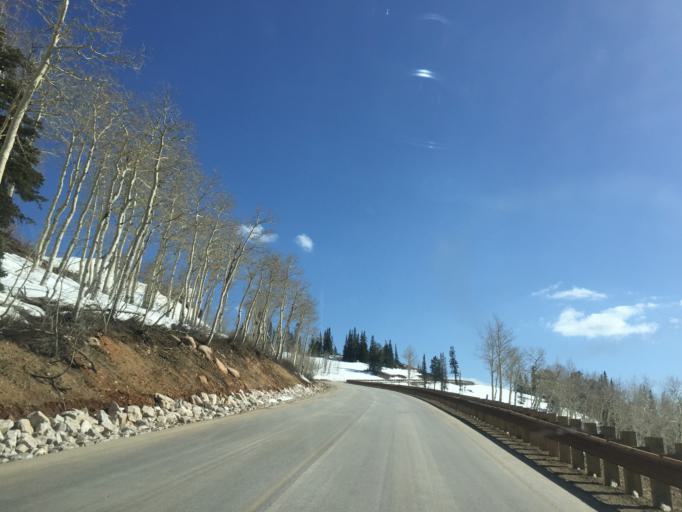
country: US
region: Utah
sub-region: Weber County
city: Wolf Creek
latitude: 41.3711
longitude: -111.7694
